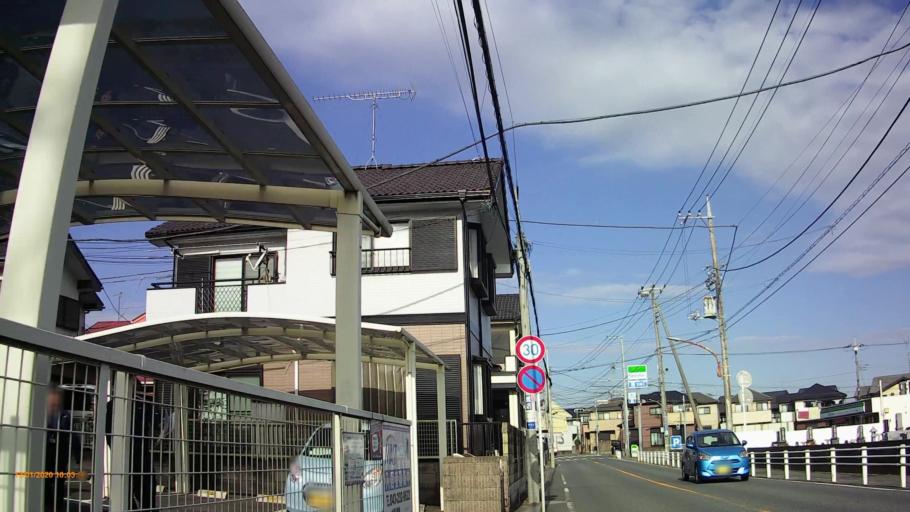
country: JP
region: Chiba
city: Yotsukaido
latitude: 35.6365
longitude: 140.1643
